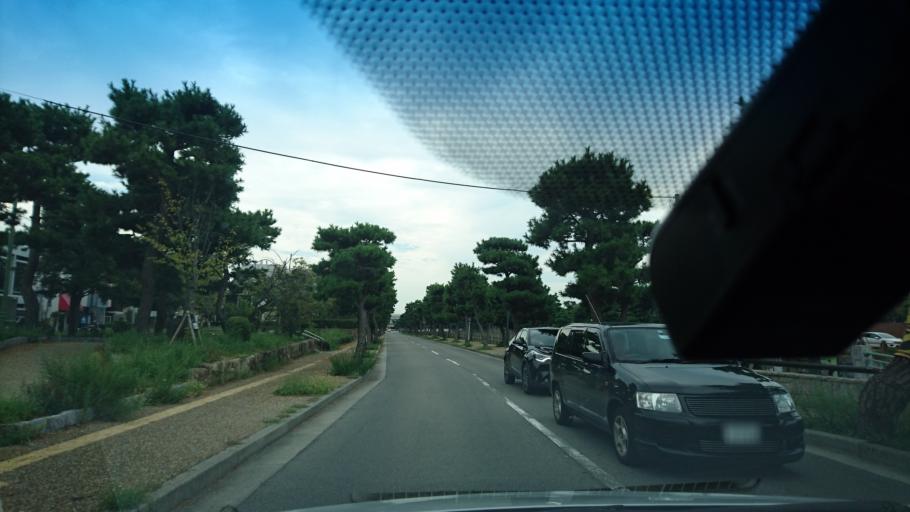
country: JP
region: Hyogo
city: Ashiya
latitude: 34.7314
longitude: 135.3029
